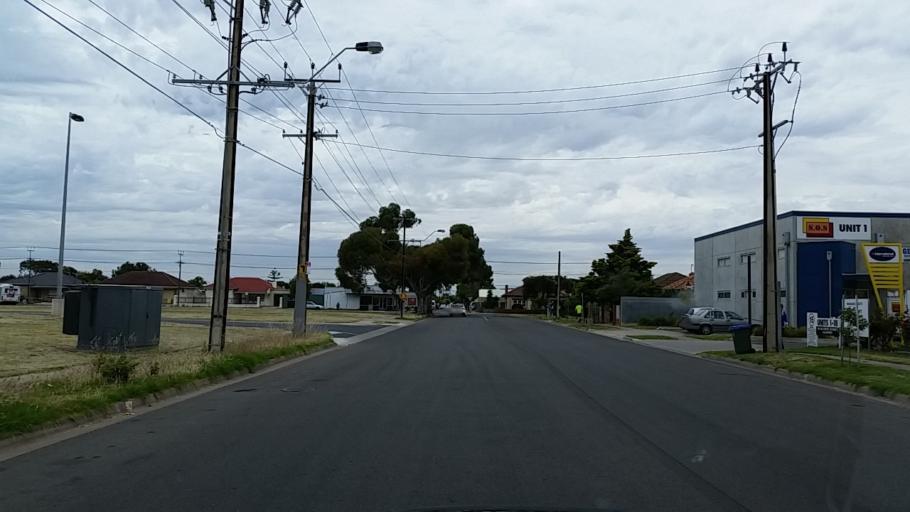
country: AU
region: South Australia
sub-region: Charles Sturt
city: Woodville North
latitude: -34.8733
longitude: 138.5520
